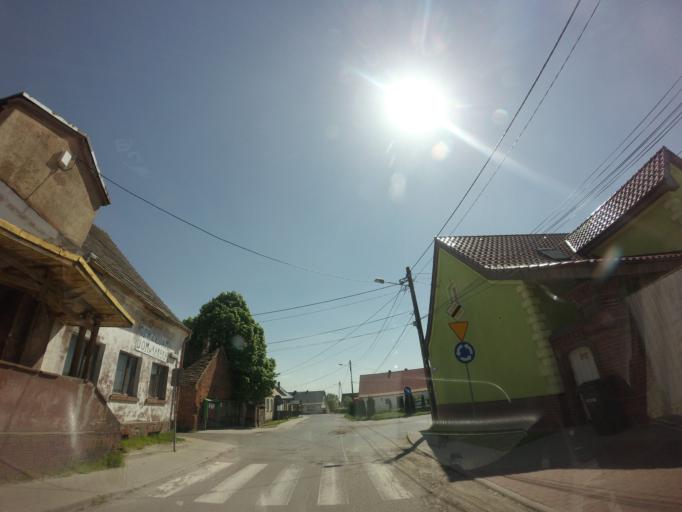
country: PL
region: West Pomeranian Voivodeship
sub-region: Powiat mysliborski
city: Nowogrodek Pomorski
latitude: 52.9112
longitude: 15.0279
